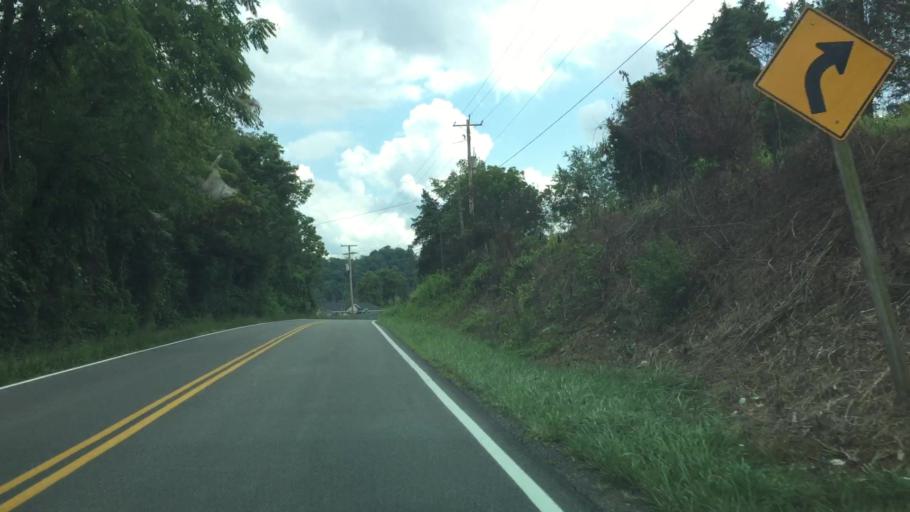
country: US
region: Virginia
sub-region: Pulaski County
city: Dublin
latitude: 37.0485
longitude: -80.7114
